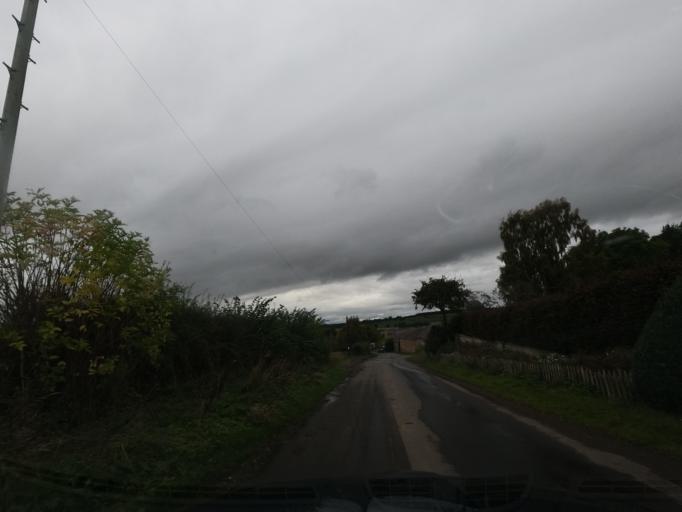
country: GB
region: England
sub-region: Northumberland
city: Ford
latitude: 55.6134
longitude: -2.0703
